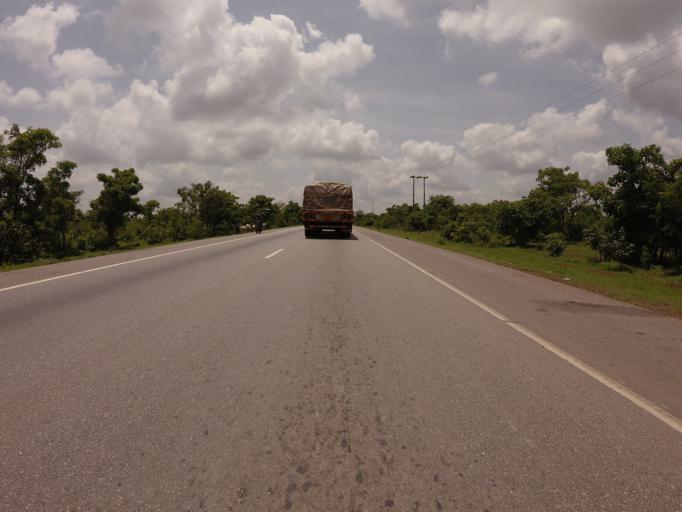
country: GH
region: Northern
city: Tamale
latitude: 9.1864
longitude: -1.0986
